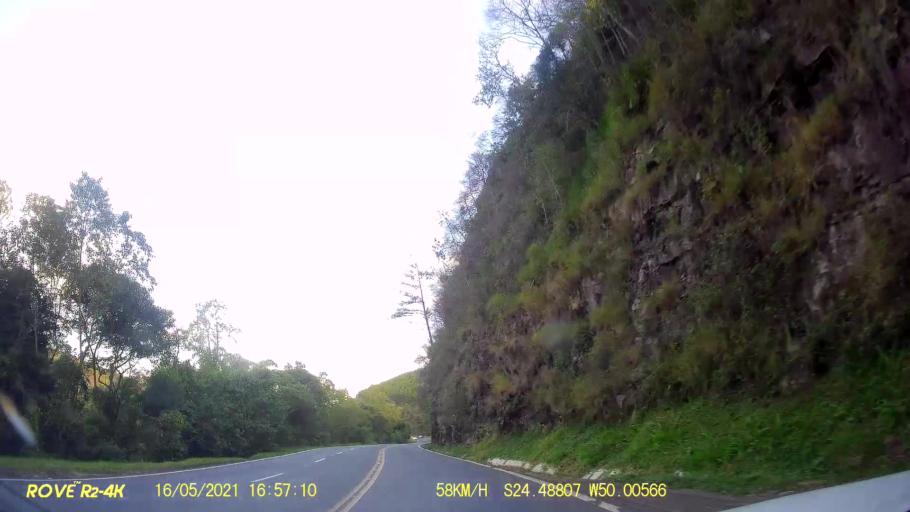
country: BR
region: Parana
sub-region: Pirai Do Sul
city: Pirai do Sul
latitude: -24.4882
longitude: -50.0055
